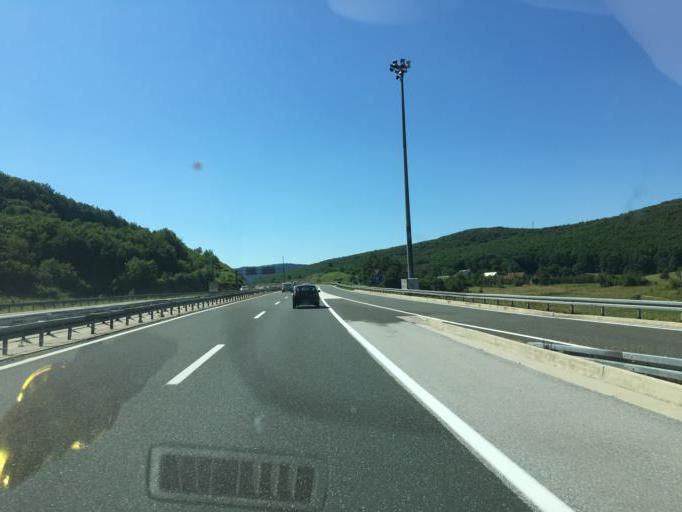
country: HR
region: Licko-Senjska
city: Otocac
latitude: 44.8899
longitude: 15.1936
